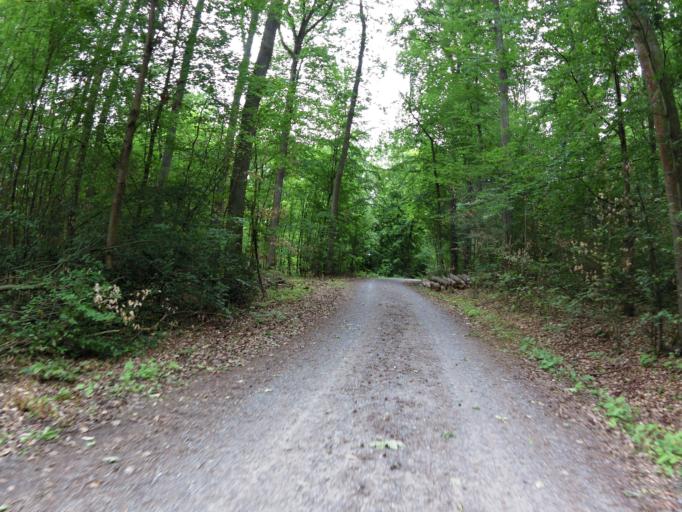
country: DE
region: Bavaria
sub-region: Regierungsbezirk Unterfranken
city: Margetshochheim
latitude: 49.8194
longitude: 9.8397
